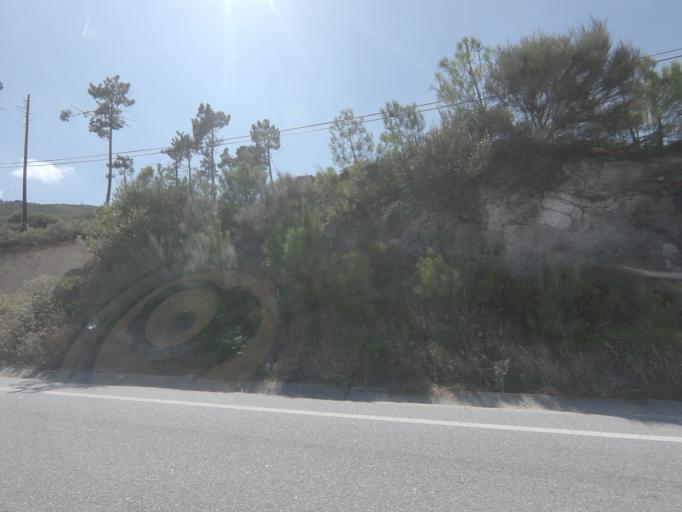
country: PT
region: Viseu
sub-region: Tarouca
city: Tarouca
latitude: 41.0049
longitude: -7.7818
